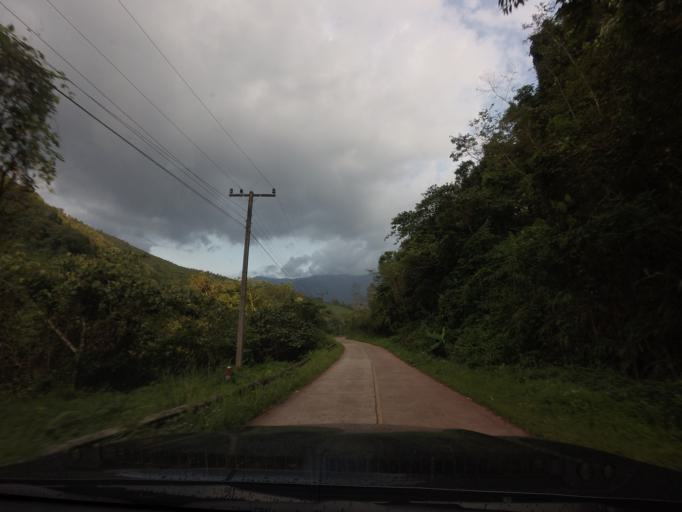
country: TH
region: Nan
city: Bo Kluea
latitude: 19.1951
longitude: 101.1920
